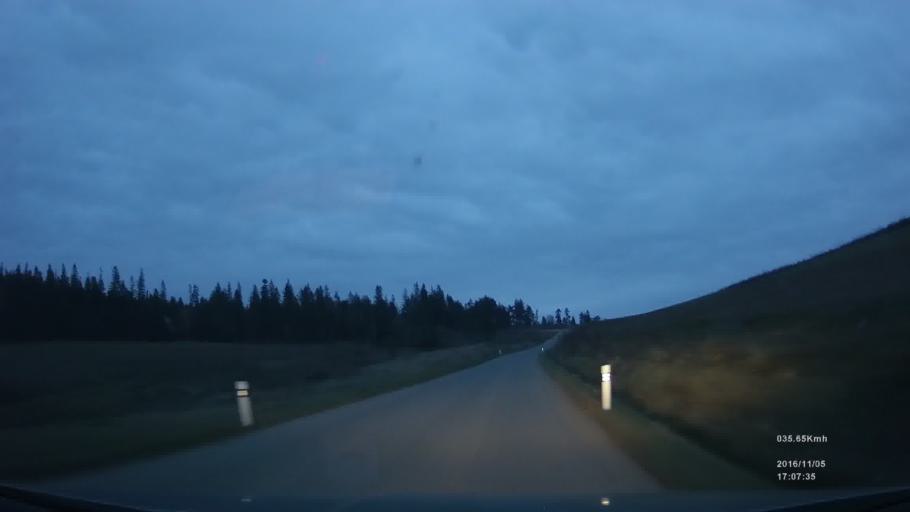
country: SK
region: Presovsky
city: Lubica
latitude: 49.0480
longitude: 20.5064
